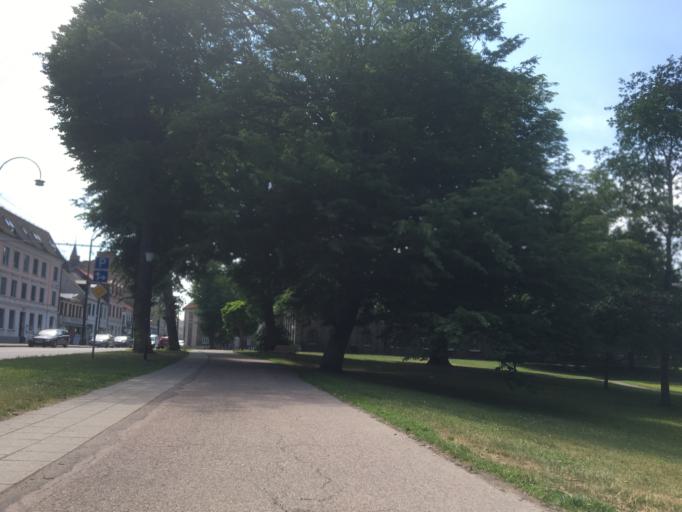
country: SE
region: Skane
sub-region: Landskrona
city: Landskrona
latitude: 55.8724
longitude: 12.8301
